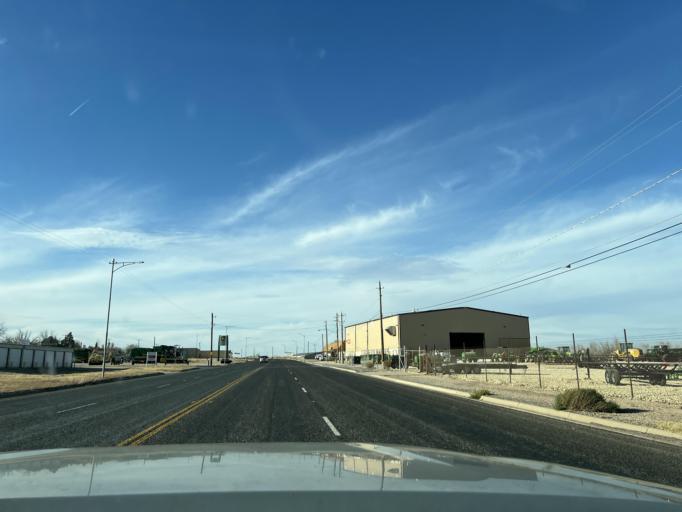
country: US
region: Texas
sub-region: Scurry County
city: Snyder
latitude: 32.7090
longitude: -100.8883
